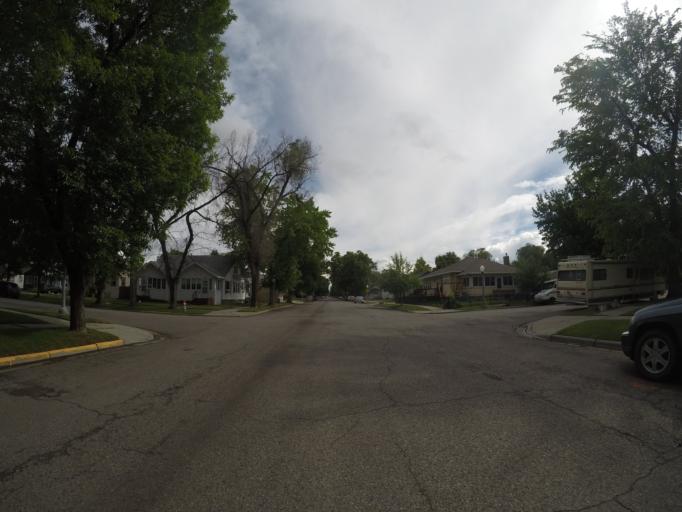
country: US
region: Montana
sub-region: Yellowstone County
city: Billings
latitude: 45.7822
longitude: -108.5230
